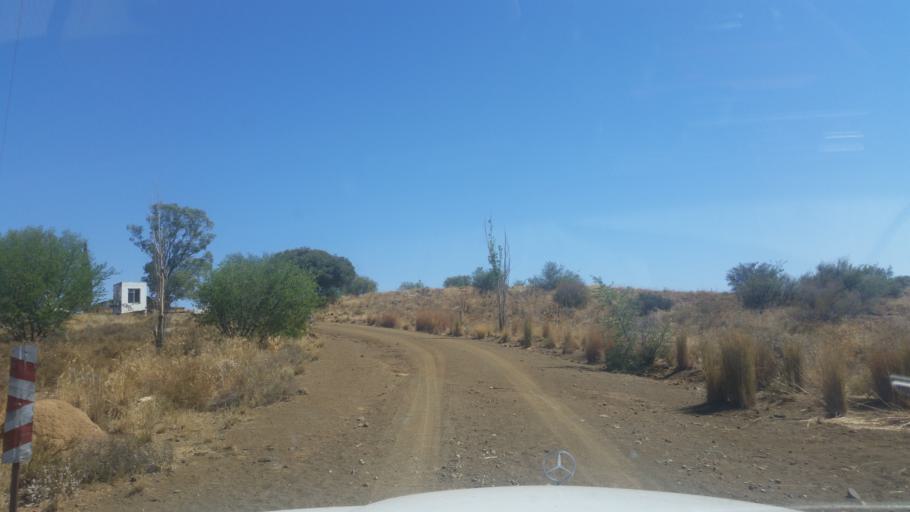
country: ZA
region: Eastern Cape
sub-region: Joe Gqabi District Municipality
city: Burgersdorp
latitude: -30.6932
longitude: 25.7777
